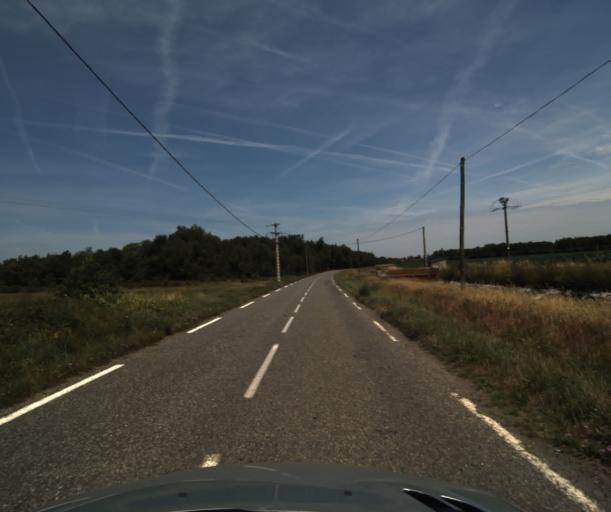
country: FR
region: Midi-Pyrenees
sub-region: Departement de la Haute-Garonne
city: Lherm
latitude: 43.4435
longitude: 1.2275
